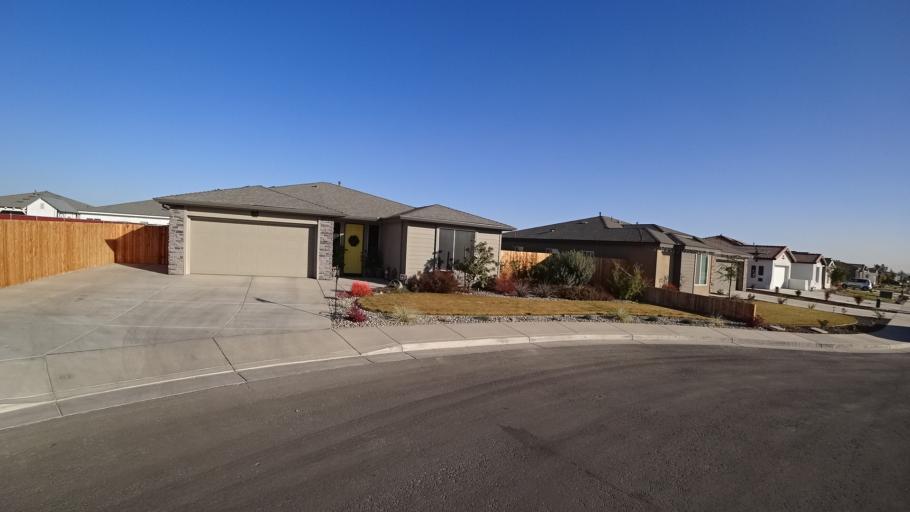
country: US
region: California
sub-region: Kern County
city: Greenfield
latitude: 35.2710
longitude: -119.0340
